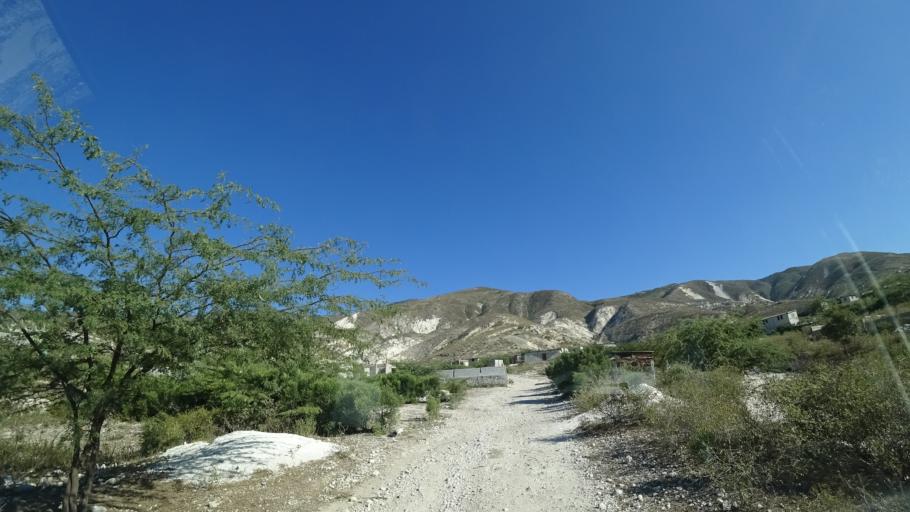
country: HT
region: Ouest
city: Croix des Bouquets
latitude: 18.6766
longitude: -72.2412
